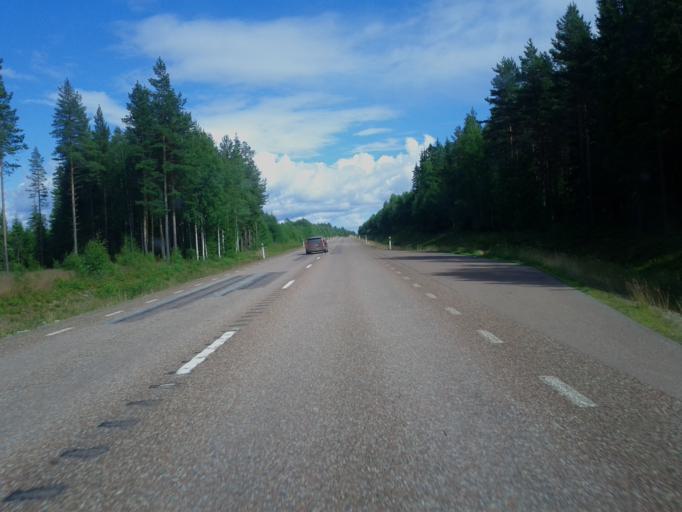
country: SE
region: Dalarna
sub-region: Rattviks Kommun
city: Raettvik
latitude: 60.8453
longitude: 15.1675
